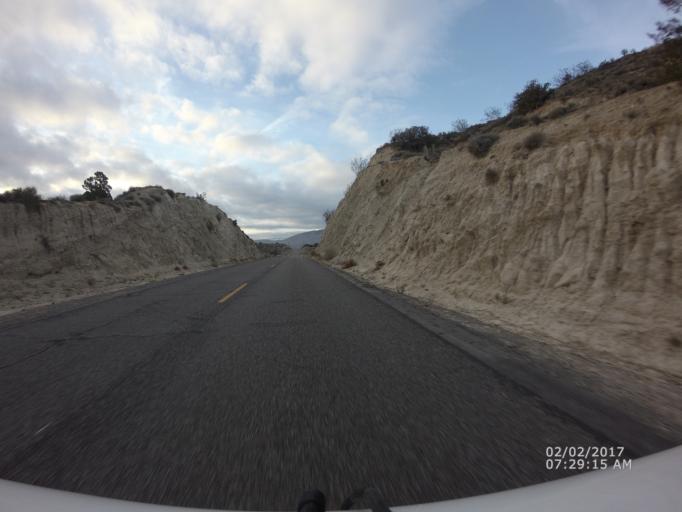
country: US
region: California
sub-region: Los Angeles County
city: Littlerock
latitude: 34.5278
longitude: -118.0453
